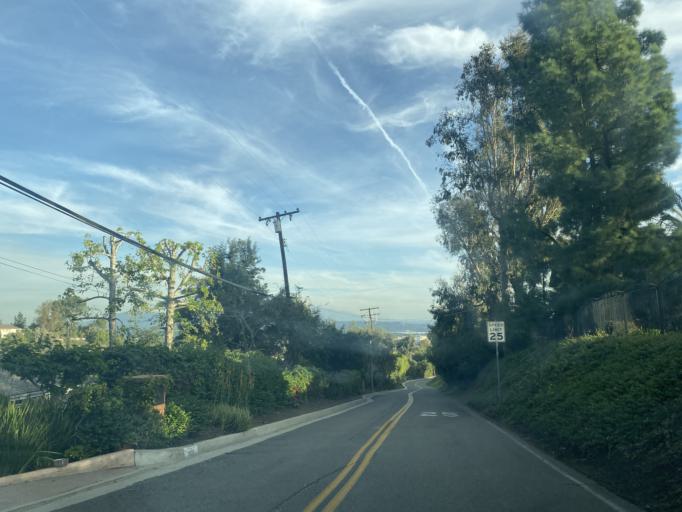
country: US
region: California
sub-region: Orange County
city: Brea
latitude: 33.8911
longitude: -117.9011
